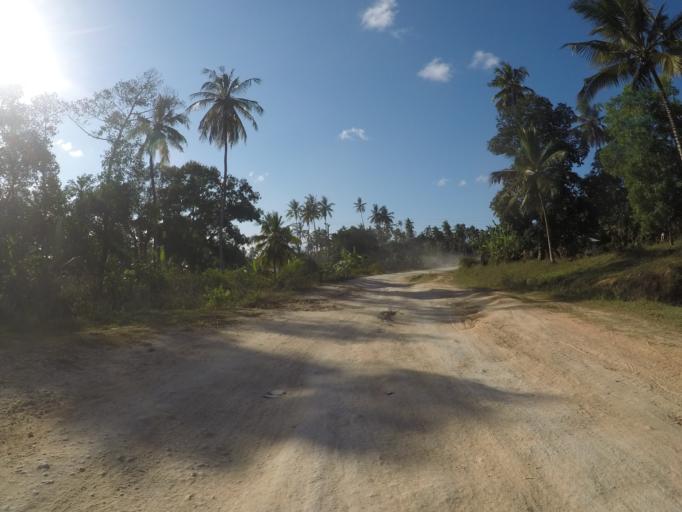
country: TZ
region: Zanzibar Central/South
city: Koani
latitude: -6.1782
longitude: 39.2835
